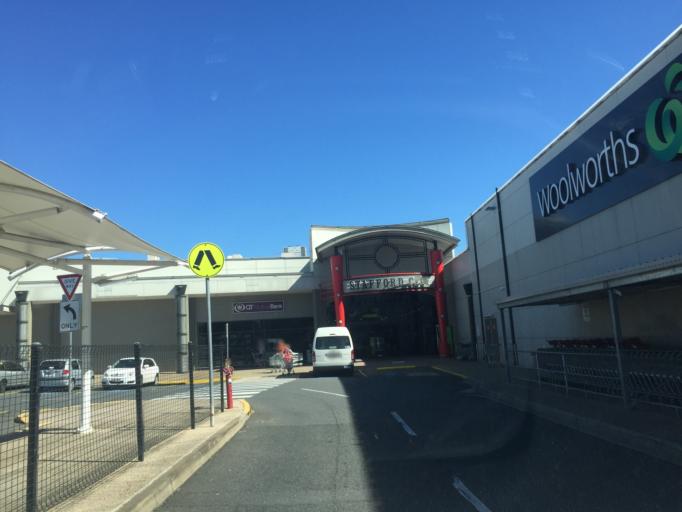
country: AU
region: Queensland
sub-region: Brisbane
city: Stafford
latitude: -27.4123
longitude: 153.0128
